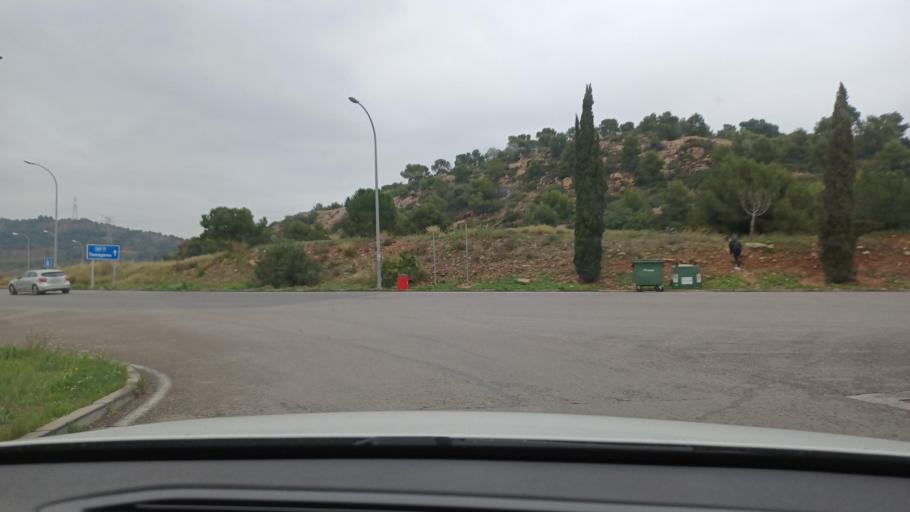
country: ES
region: Valencia
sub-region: Provincia de Valencia
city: Petres
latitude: 39.6514
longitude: -0.3016
